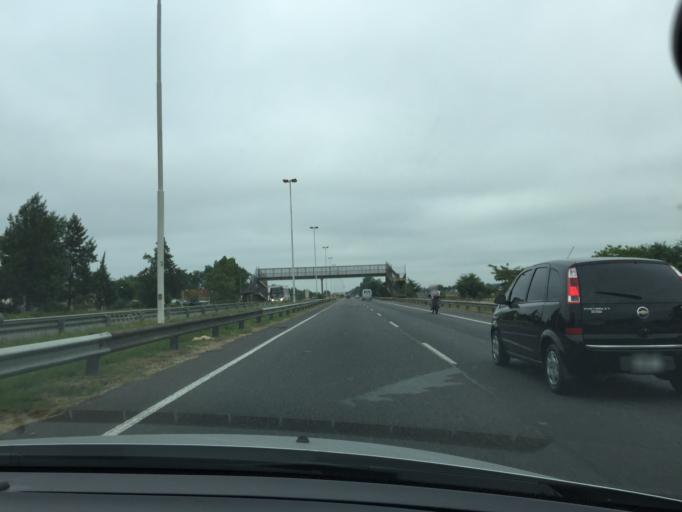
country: AR
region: Buenos Aires
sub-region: Partido de Ezeiza
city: Ezeiza
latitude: -34.8414
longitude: -58.5275
